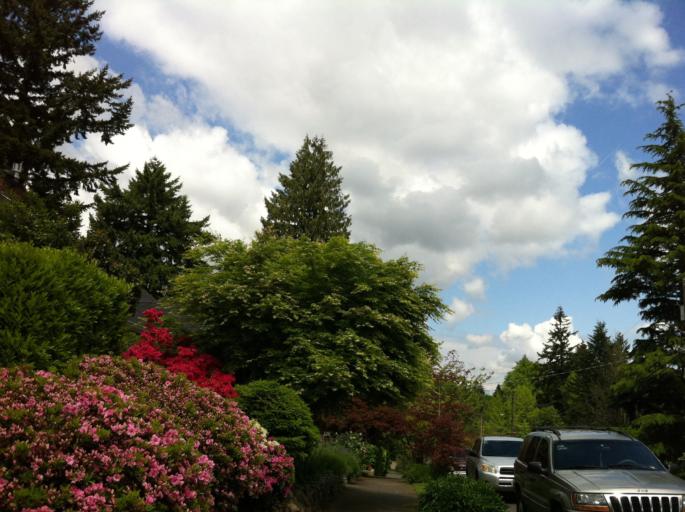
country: US
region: Oregon
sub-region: Clackamas County
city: Lake Oswego
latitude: 45.4647
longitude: -122.6900
